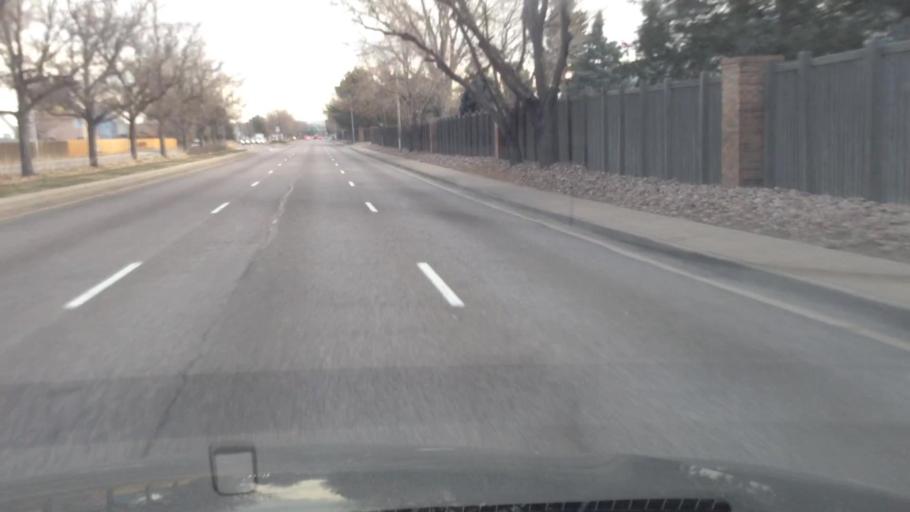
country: US
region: Colorado
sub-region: Adams County
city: Aurora
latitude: 39.6747
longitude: -104.8171
